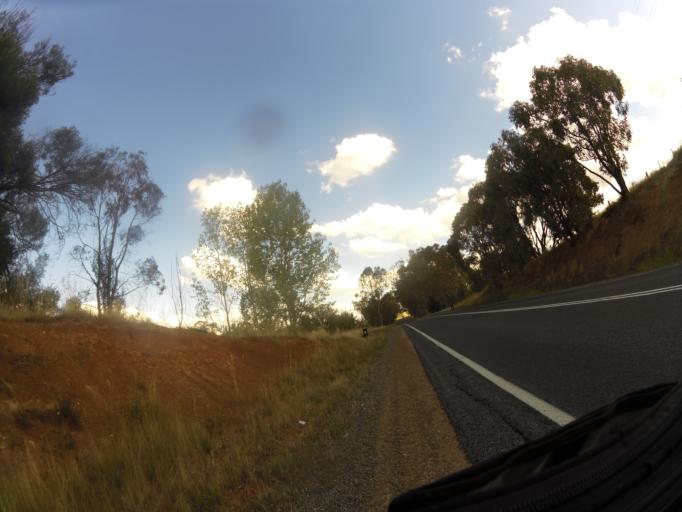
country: AU
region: Victoria
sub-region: Mansfield
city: Mansfield
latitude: -36.9374
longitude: 145.9991
